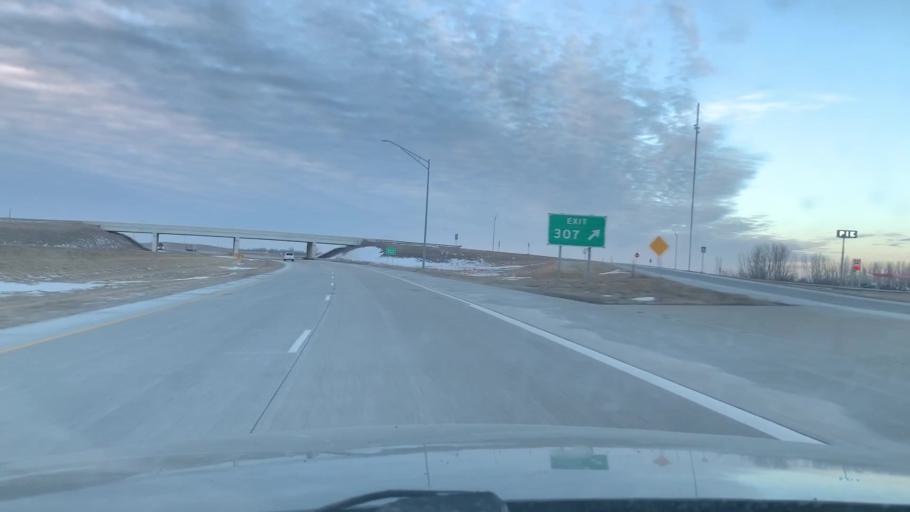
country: US
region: North Dakota
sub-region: Barnes County
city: Valley City
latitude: 46.9177
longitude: -97.6803
